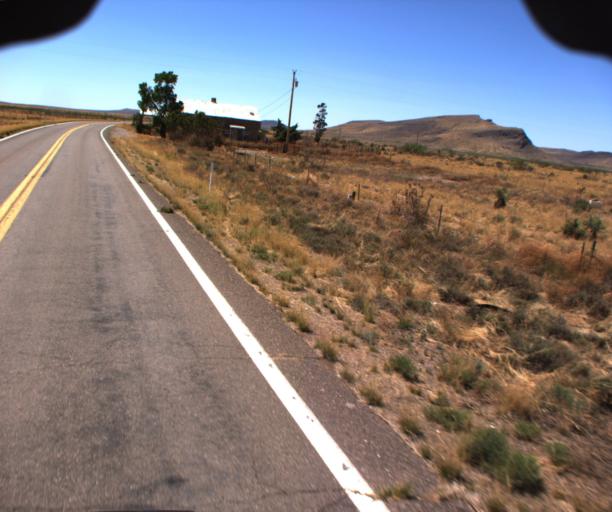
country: US
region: Arizona
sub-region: Cochise County
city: Douglas
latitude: 31.6930
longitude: -109.1310
